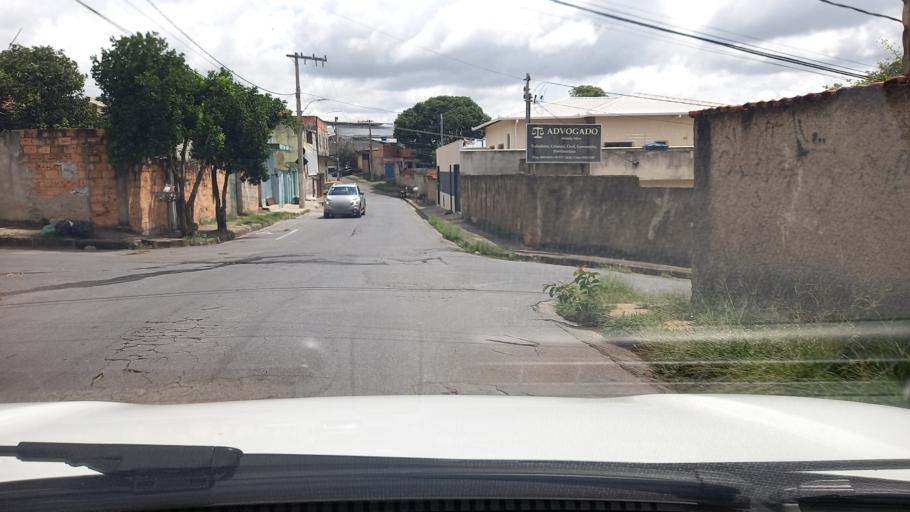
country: BR
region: Minas Gerais
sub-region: Contagem
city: Contagem
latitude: -19.9006
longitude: -44.0196
